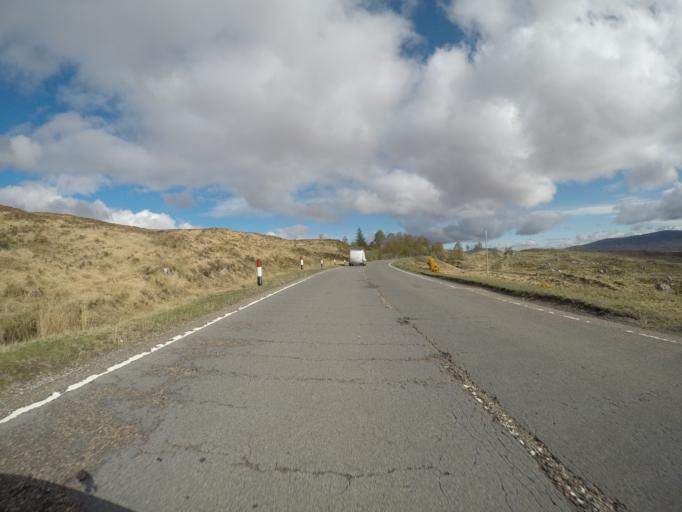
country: GB
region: Scotland
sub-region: Highland
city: Spean Bridge
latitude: 56.6190
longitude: -4.7661
